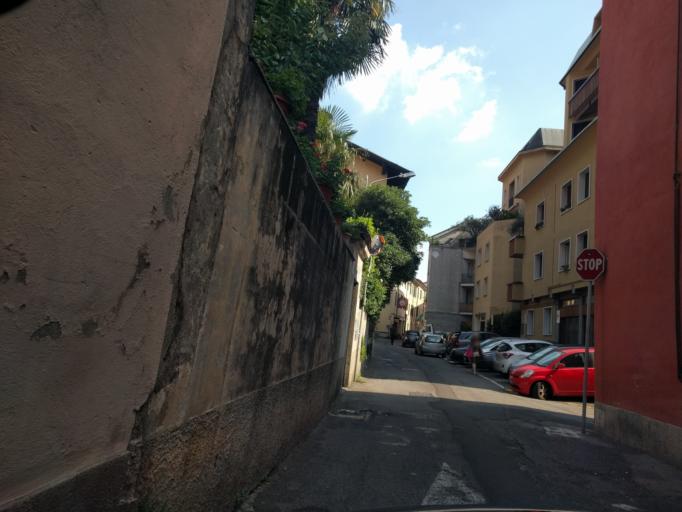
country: IT
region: Lombardy
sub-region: Provincia di Como
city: Brunate
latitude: 45.8167
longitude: 9.0836
